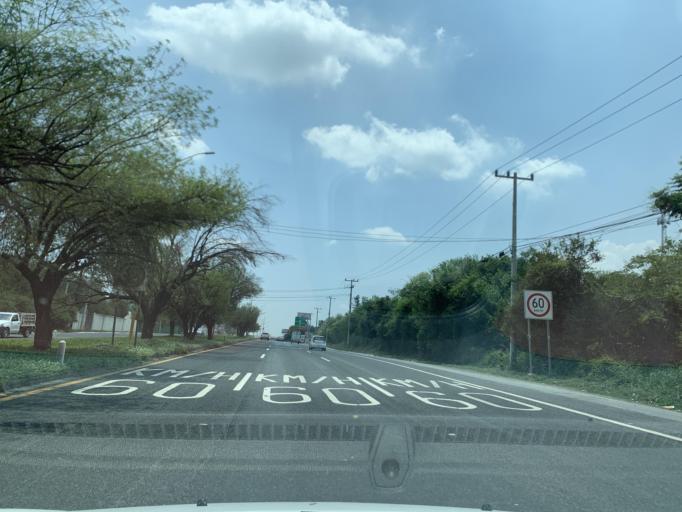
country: MX
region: Nuevo Leon
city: Santiago
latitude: 25.4973
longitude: -100.1897
